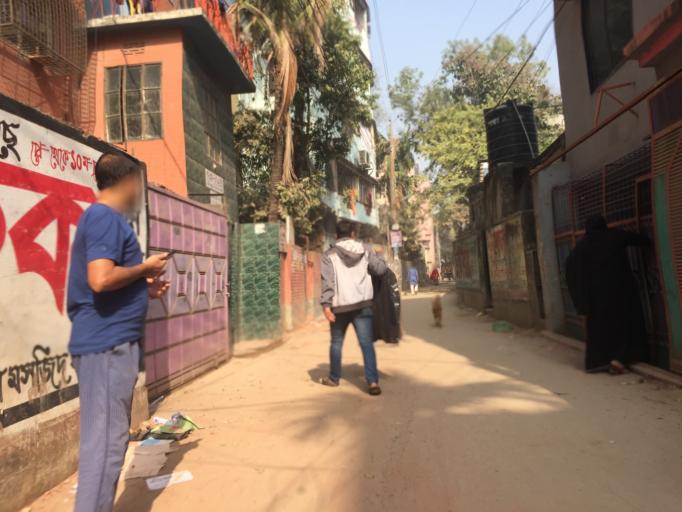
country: BD
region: Dhaka
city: Azimpur
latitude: 23.7911
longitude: 90.3646
